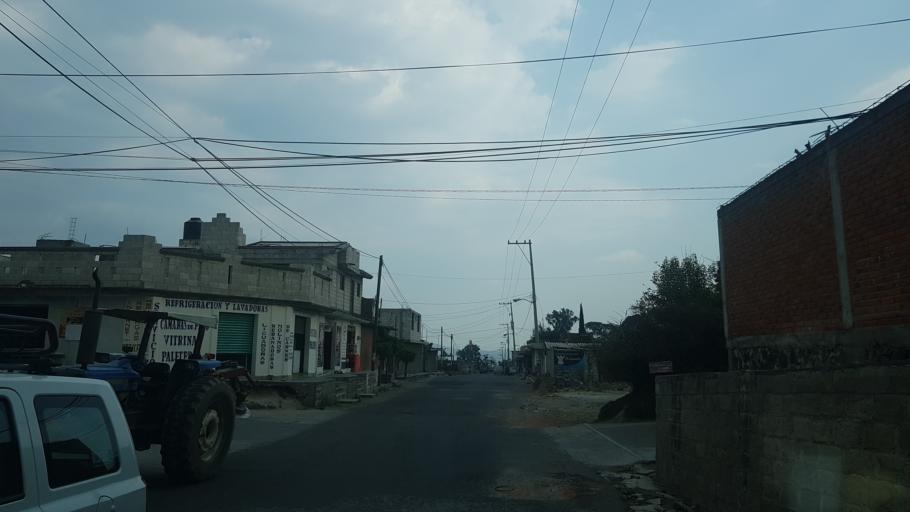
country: MX
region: Puebla
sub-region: Santa Isabel Cholula
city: Santa Ana Acozautla
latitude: 18.9466
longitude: -98.3949
